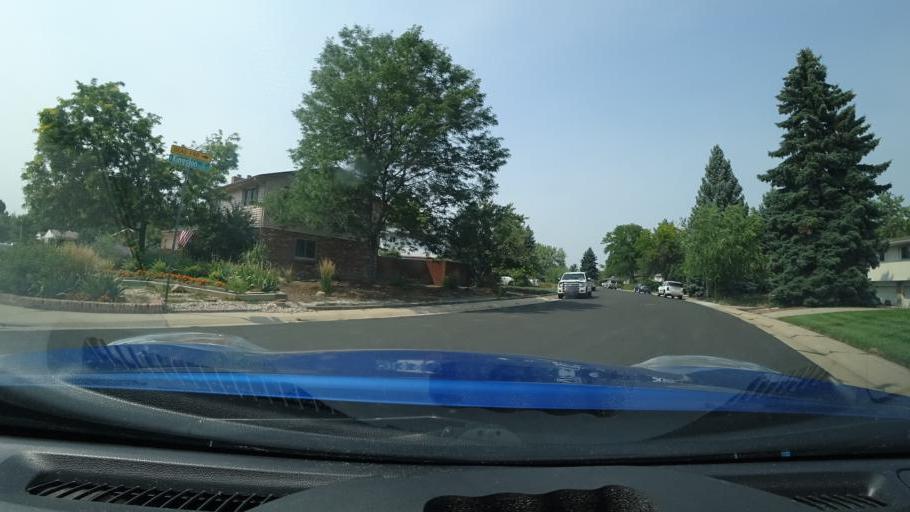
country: US
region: Colorado
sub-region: Adams County
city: Aurora
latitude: 39.6730
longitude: -104.8589
